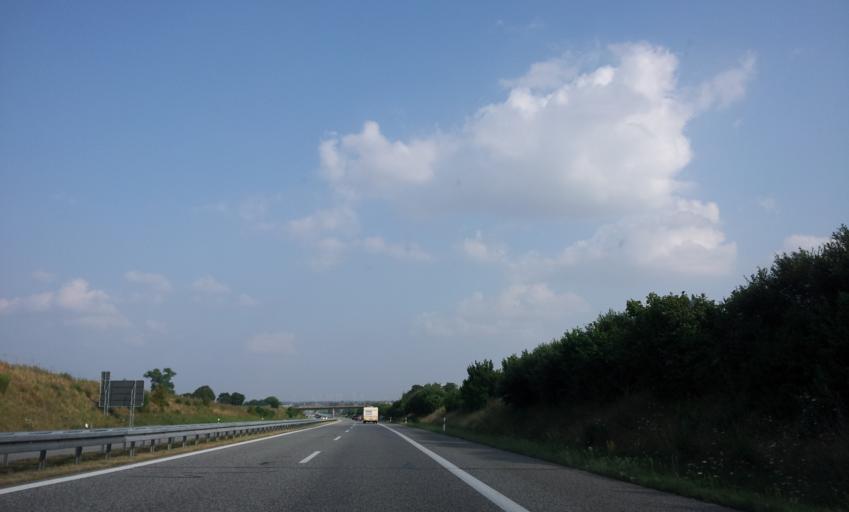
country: DE
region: Mecklenburg-Vorpommern
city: Pasewalk
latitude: 53.4891
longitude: 13.9228
